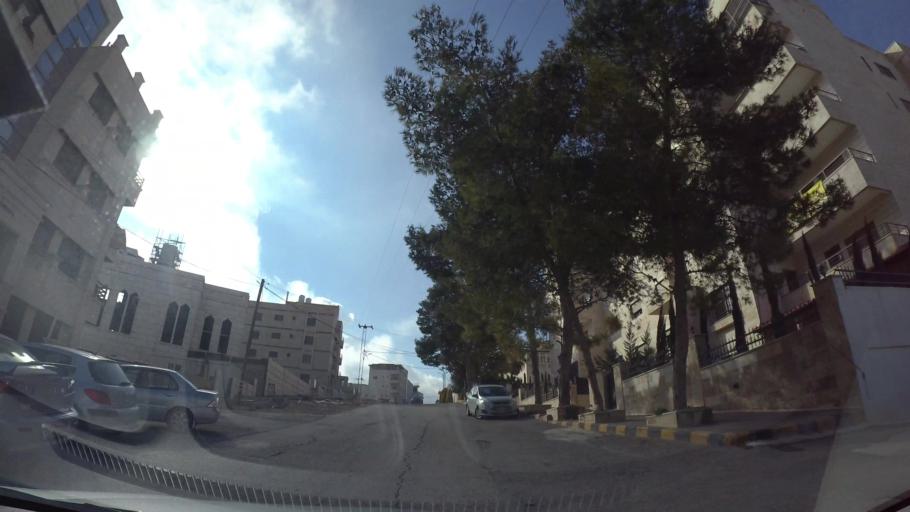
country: JO
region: Amman
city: Al Jubayhah
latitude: 32.0405
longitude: 35.8731
